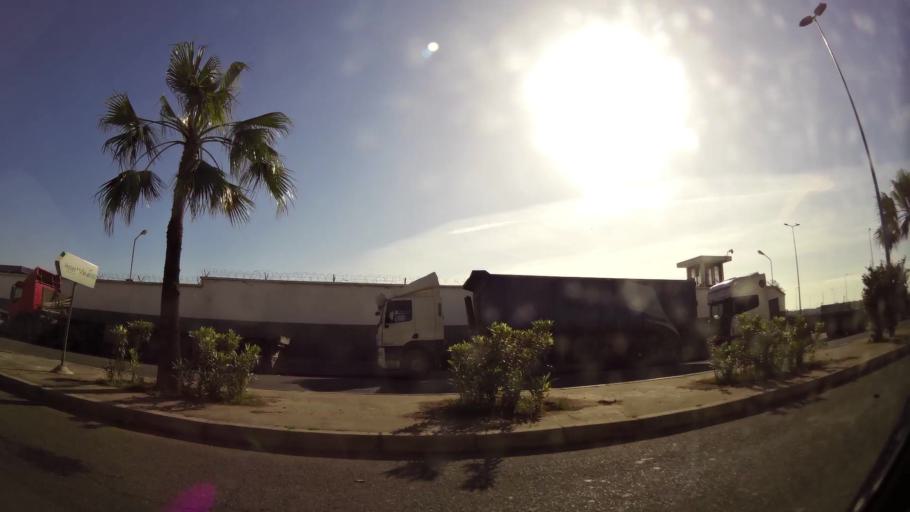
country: MA
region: Grand Casablanca
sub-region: Casablanca
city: Casablanca
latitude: 33.6013
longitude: -7.5783
